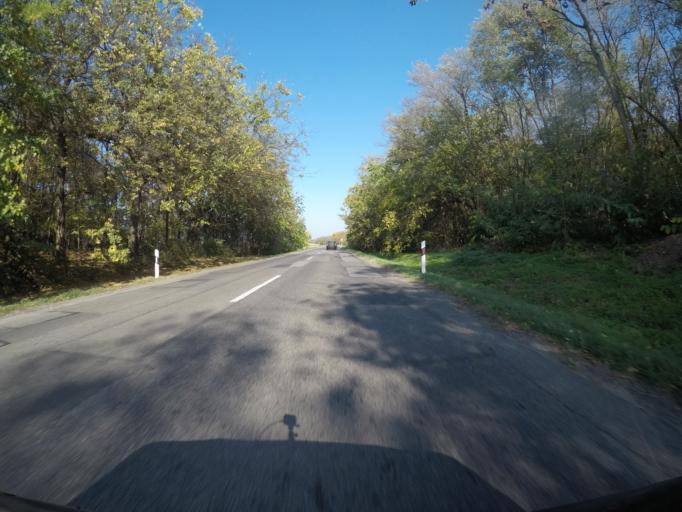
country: HU
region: Tolna
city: Szedres
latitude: 46.4590
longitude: 18.6877
